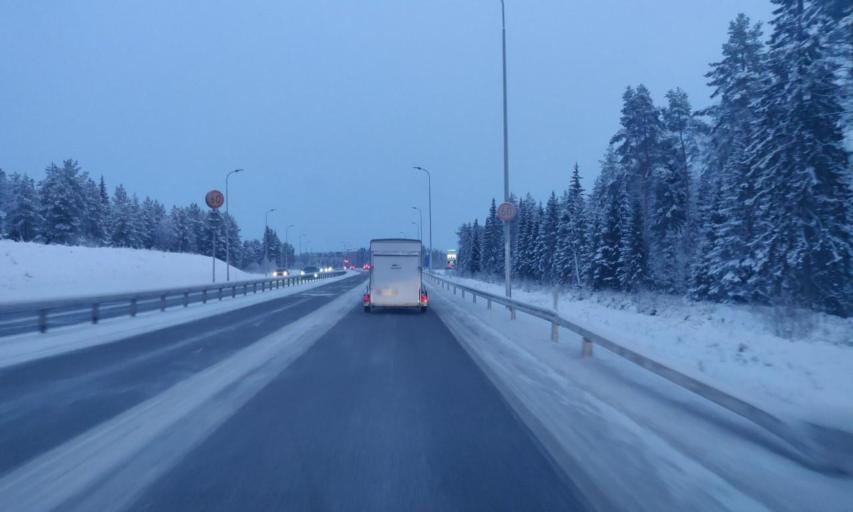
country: FI
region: Northern Ostrobothnia
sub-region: Oulu
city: Kempele
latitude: 64.9822
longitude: 25.5556
